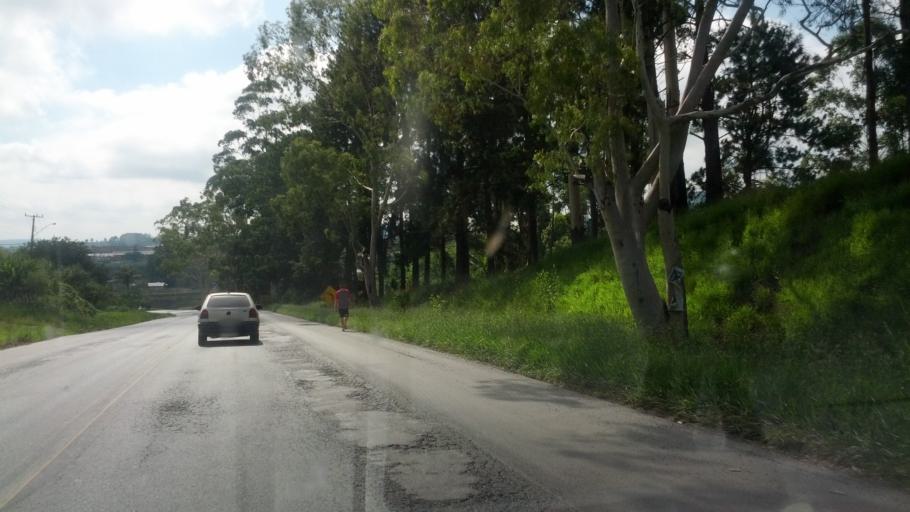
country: BR
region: Santa Catarina
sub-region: Rio Do Sul
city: Rio do Sul
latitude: -27.2596
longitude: -49.9223
